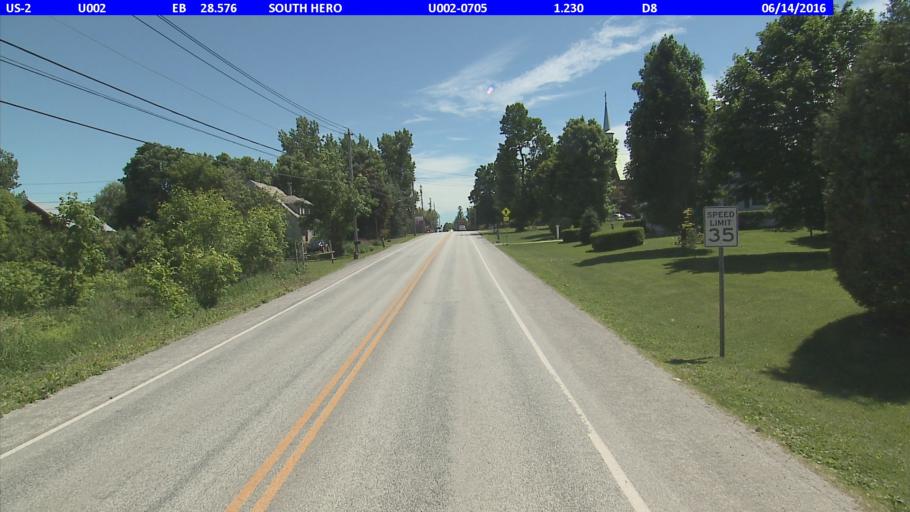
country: US
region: New York
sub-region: Clinton County
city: Cumberland Head
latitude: 44.6634
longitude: -73.3224
